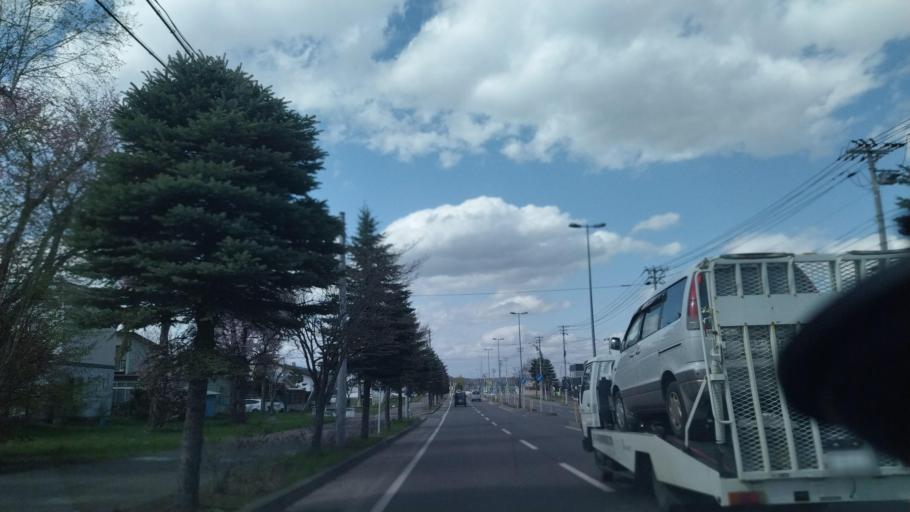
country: JP
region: Hokkaido
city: Obihiro
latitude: 42.9210
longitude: 143.1440
